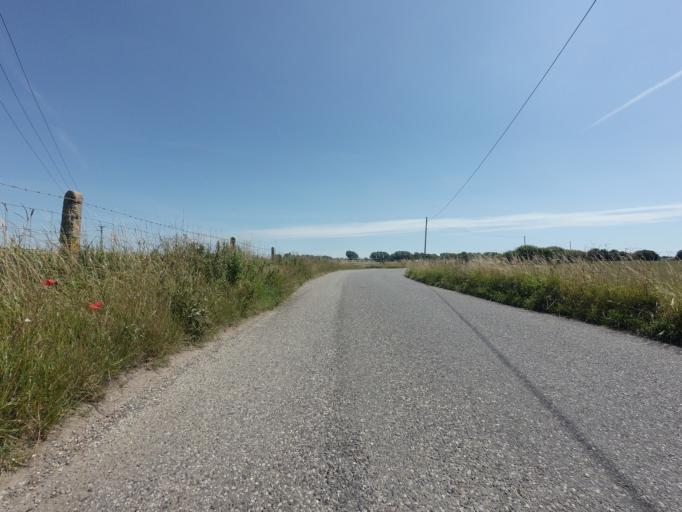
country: GB
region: England
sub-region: Kent
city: Lydd
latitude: 50.9641
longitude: 0.9006
